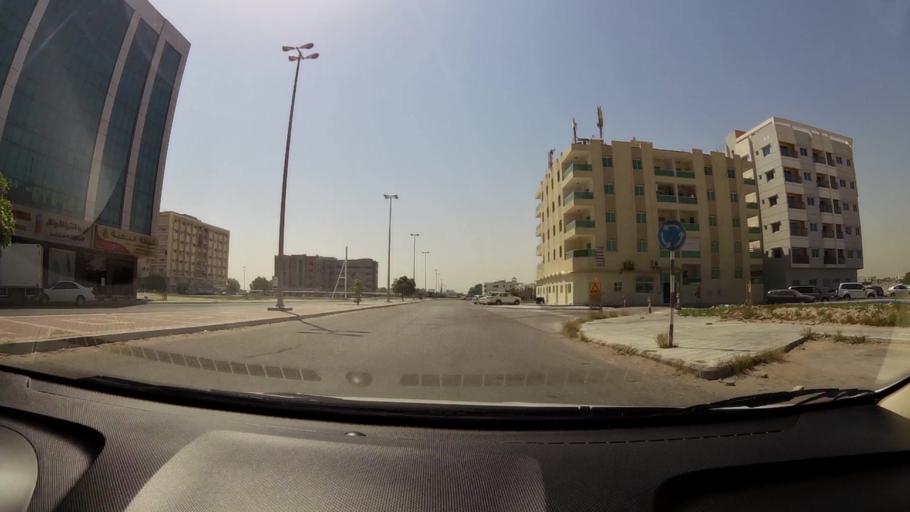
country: AE
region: Umm al Qaywayn
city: Umm al Qaywayn
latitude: 25.5764
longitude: 55.5578
